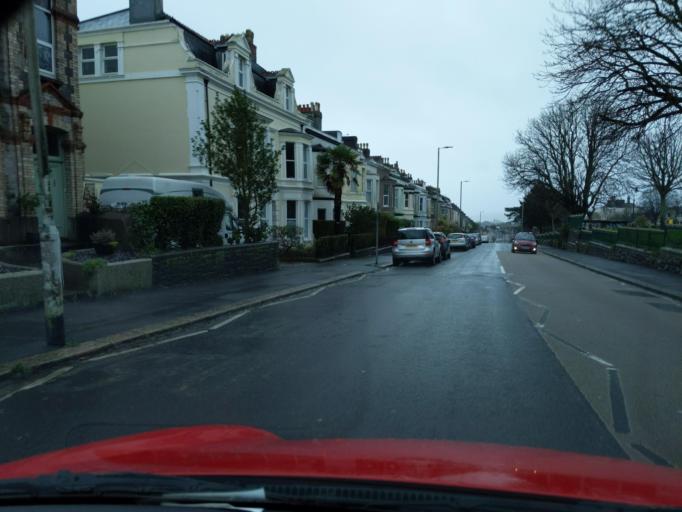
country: GB
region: England
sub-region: Plymouth
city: Plymouth
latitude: 50.3781
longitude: -4.1250
